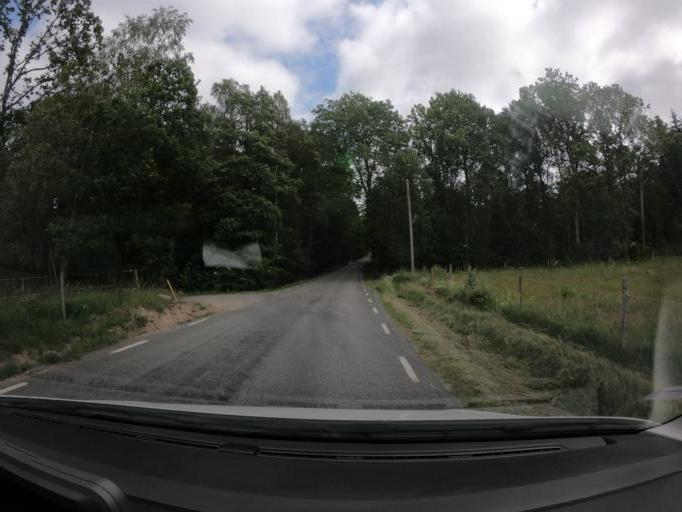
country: SE
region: Skane
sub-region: Hassleholms Kommun
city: Tormestorp
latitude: 56.1344
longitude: 13.6450
